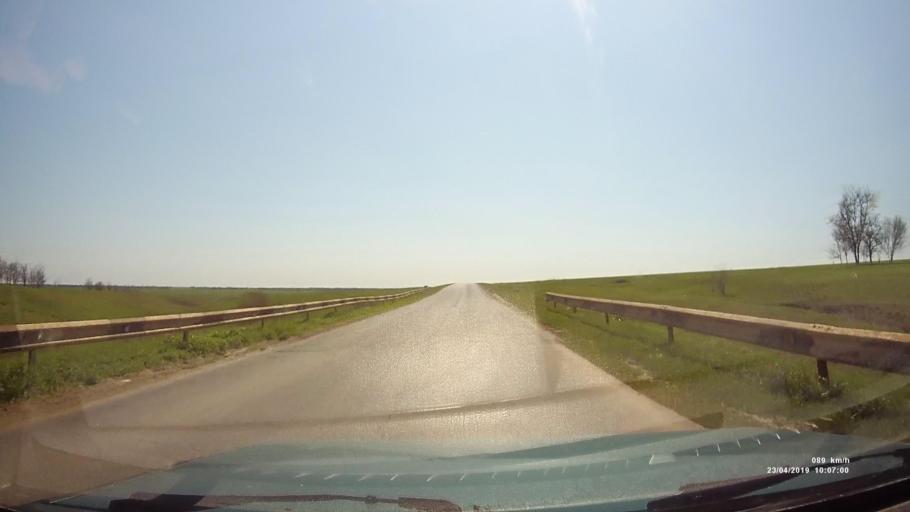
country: RU
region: Rostov
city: Sovetskoye
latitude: 46.7283
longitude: 42.2467
